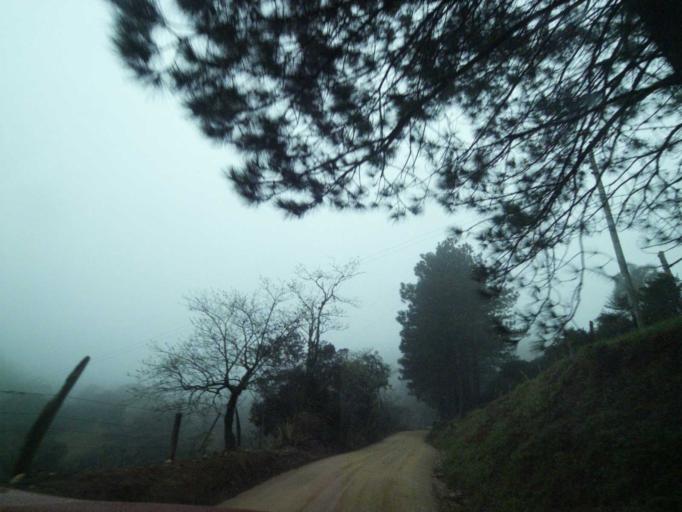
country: BR
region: Santa Catarina
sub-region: Anitapolis
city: Anitapolis
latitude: -27.9130
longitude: -49.1114
